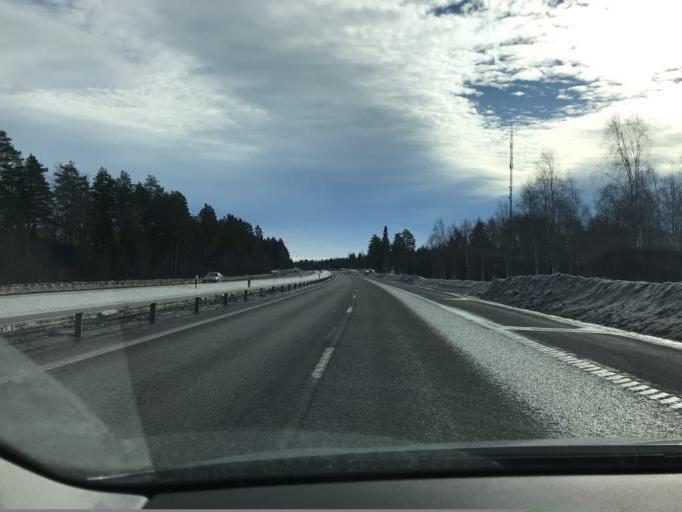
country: SE
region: Norrbotten
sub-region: Lulea Kommun
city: Gammelstad
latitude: 65.6271
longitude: 22.0493
